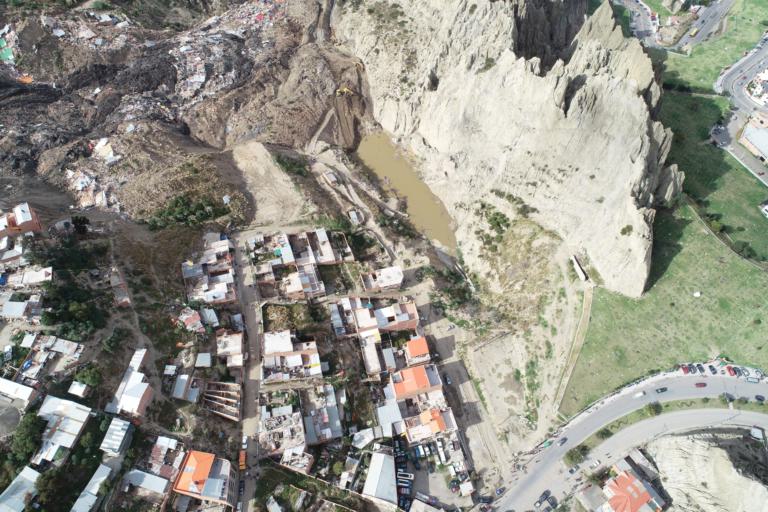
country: BO
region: La Paz
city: La Paz
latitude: -16.5215
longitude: -68.1235
